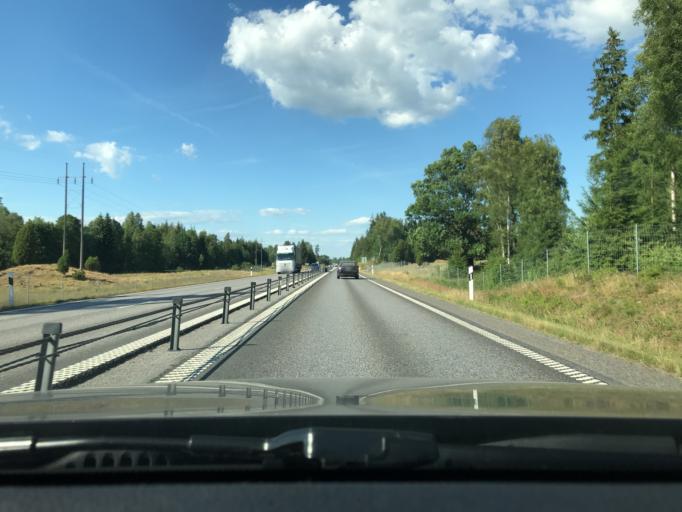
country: SE
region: Kronoberg
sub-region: Almhults Kommun
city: AElmhult
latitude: 56.5094
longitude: 14.1289
